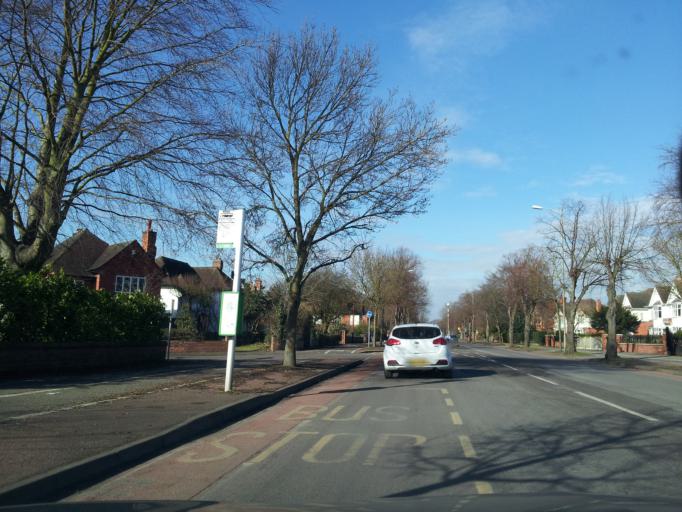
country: GB
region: England
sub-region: Nottinghamshire
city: Newark on Trent
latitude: 53.0677
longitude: -0.7959
